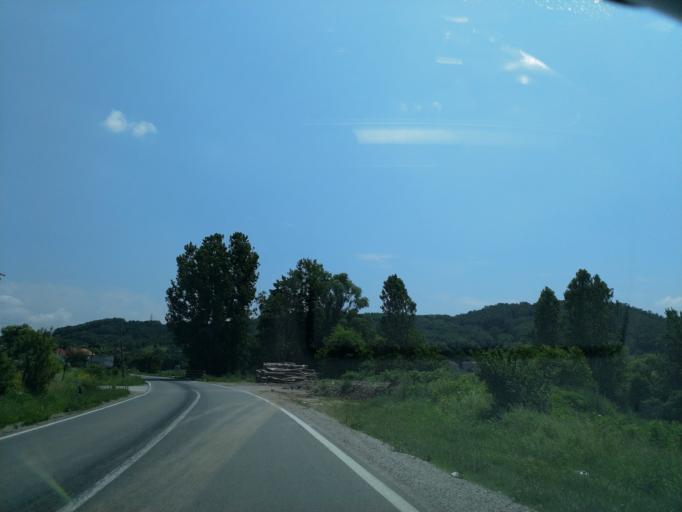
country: RS
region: Central Serbia
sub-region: Toplicki Okrug
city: Blace
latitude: 43.3074
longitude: 21.2483
